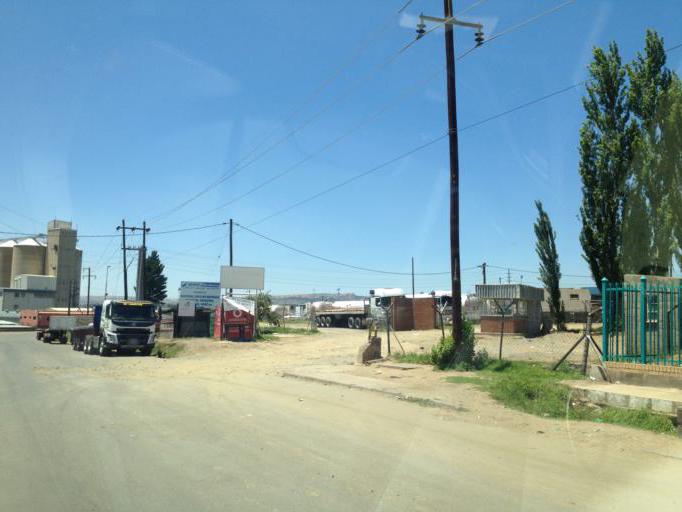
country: LS
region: Maseru
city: Maseru
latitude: -29.2971
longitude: 27.4780
